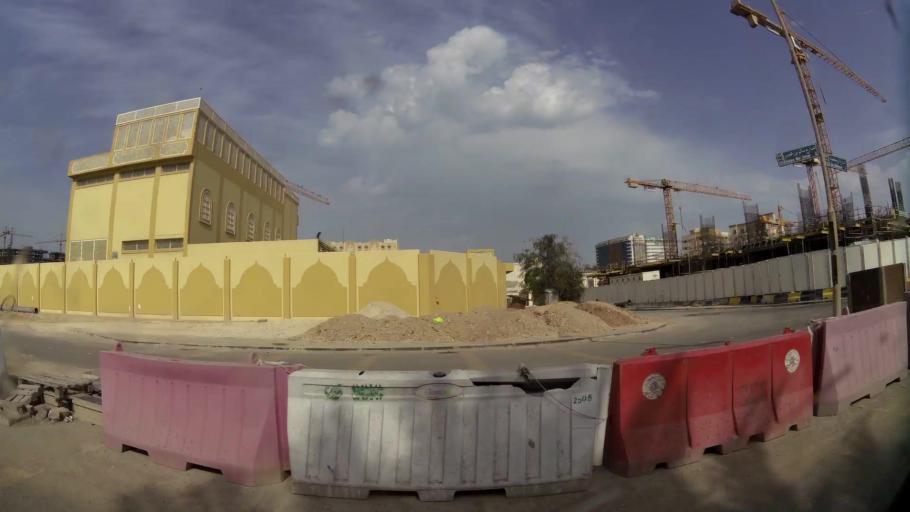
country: QA
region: Baladiyat ad Dawhah
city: Doha
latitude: 25.2800
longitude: 51.5157
